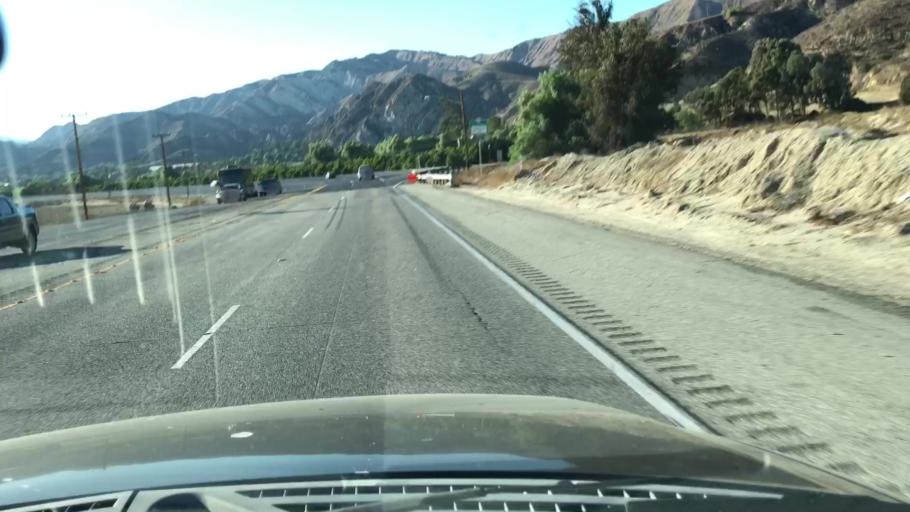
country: US
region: California
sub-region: Ventura County
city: Piru
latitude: 34.4098
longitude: -118.7790
